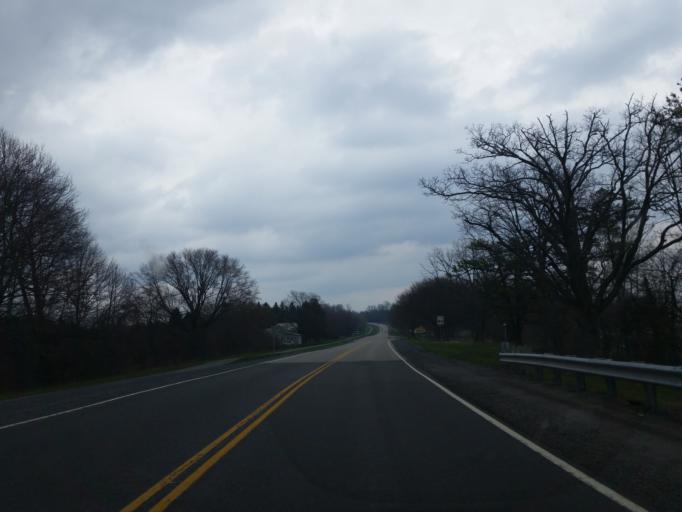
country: CA
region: Ontario
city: Brockville
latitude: 44.4863
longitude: -75.8271
